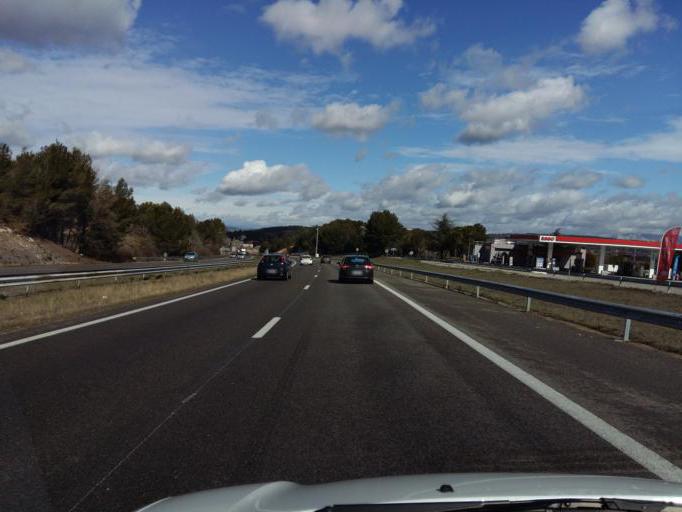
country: FR
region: Provence-Alpes-Cote d'Azur
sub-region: Departement des Bouches-du-Rhone
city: Cabries
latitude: 43.4332
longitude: 5.3947
